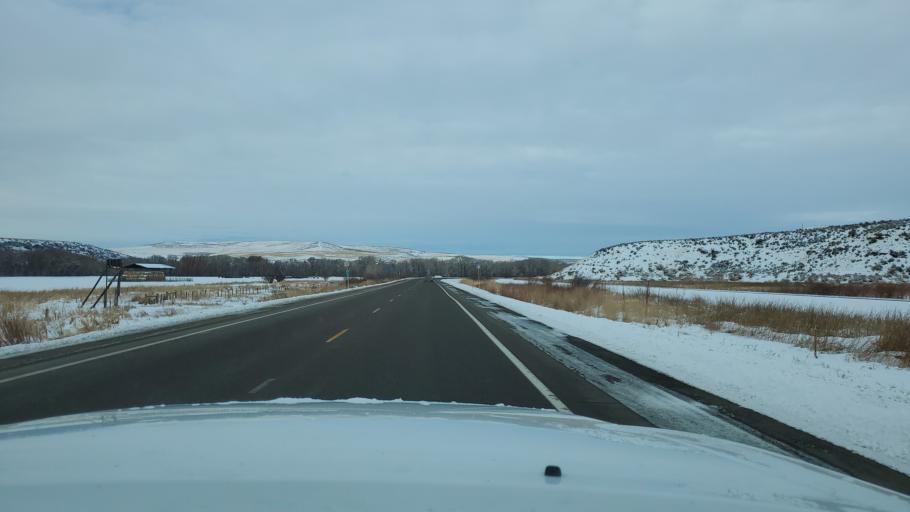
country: US
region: Colorado
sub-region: Routt County
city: Hayden
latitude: 40.4934
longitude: -107.3616
